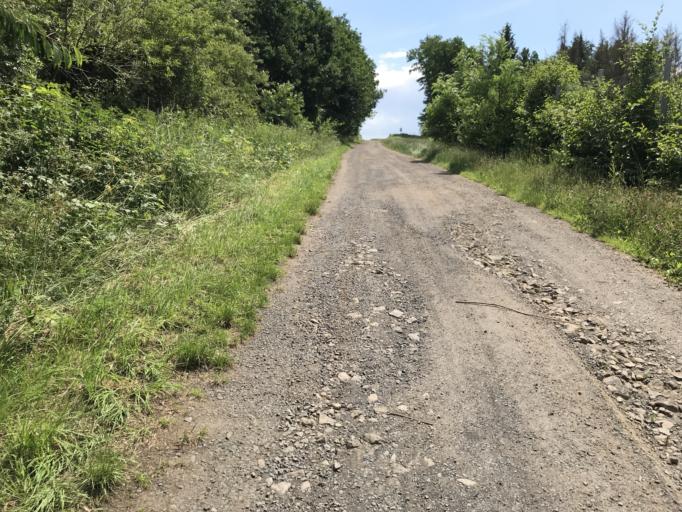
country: DE
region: Hesse
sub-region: Regierungsbezirk Giessen
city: Hungen
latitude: 50.4739
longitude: 8.9187
